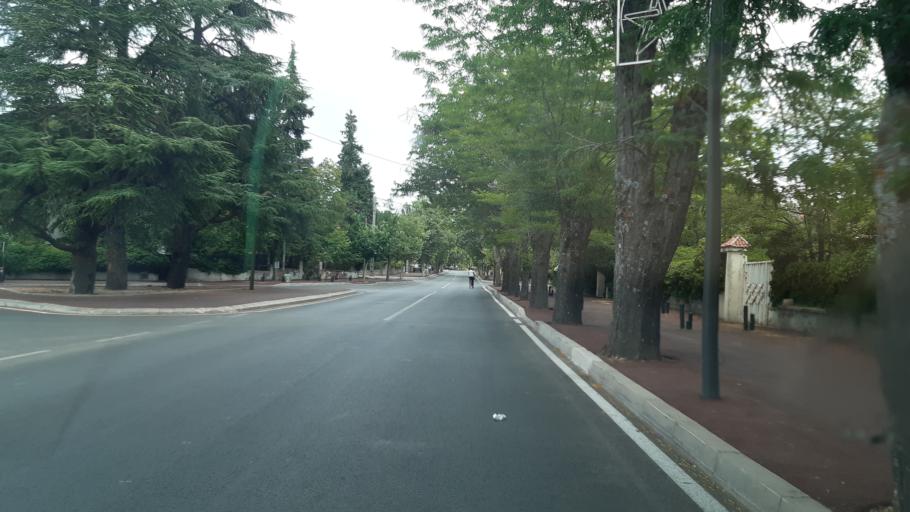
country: MA
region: Meknes-Tafilalet
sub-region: Ifrane
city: Ifrane
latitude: 33.5239
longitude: -5.1105
